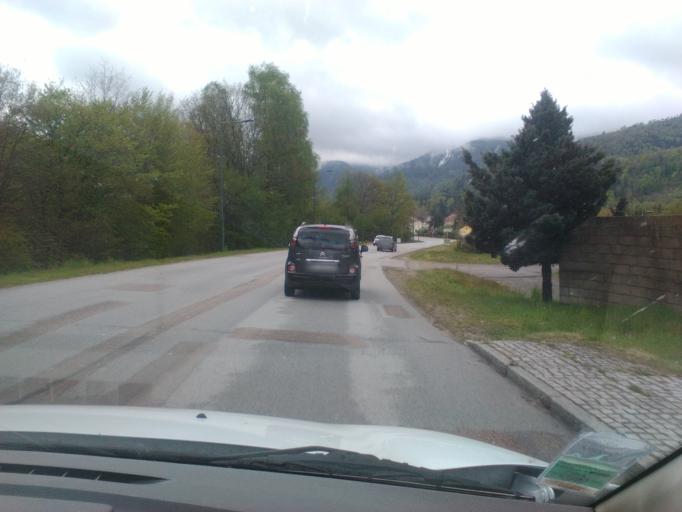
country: FR
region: Lorraine
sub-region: Departement des Vosges
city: Vagney
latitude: 47.9749
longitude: 6.7280
